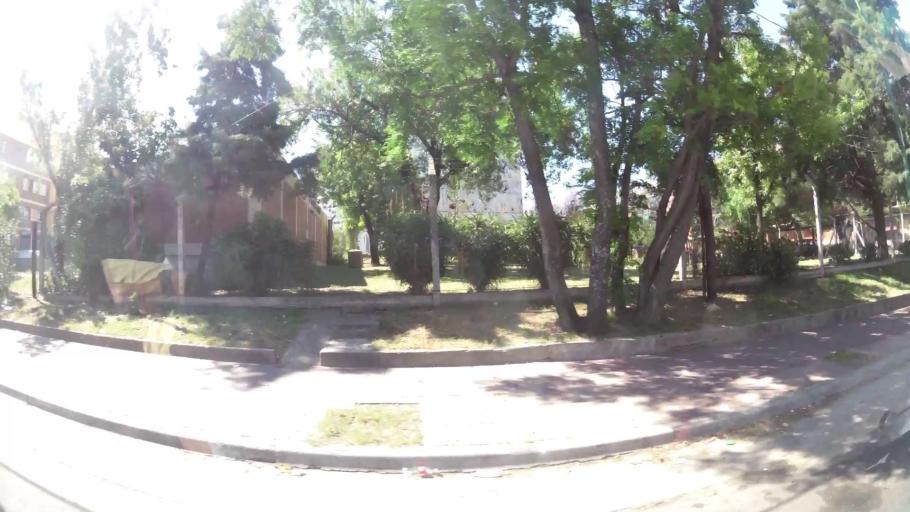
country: AR
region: Cordoba
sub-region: Departamento de Capital
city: Cordoba
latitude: -31.4081
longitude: -64.1576
